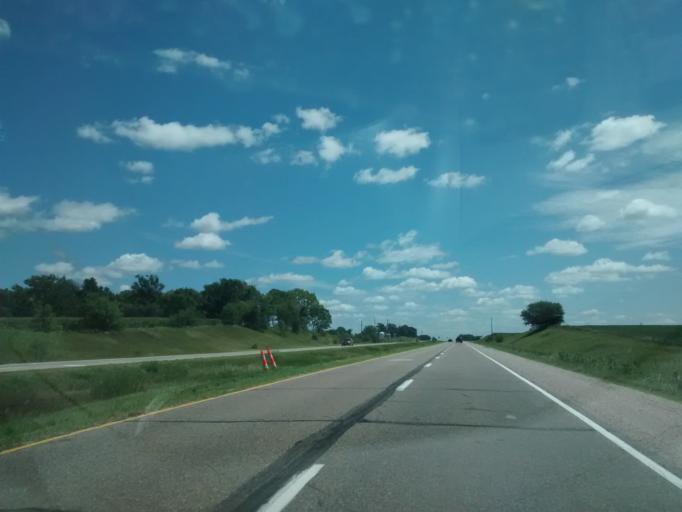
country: US
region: Iowa
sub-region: Woodbury County
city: Moville
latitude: 42.4749
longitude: -96.1395
